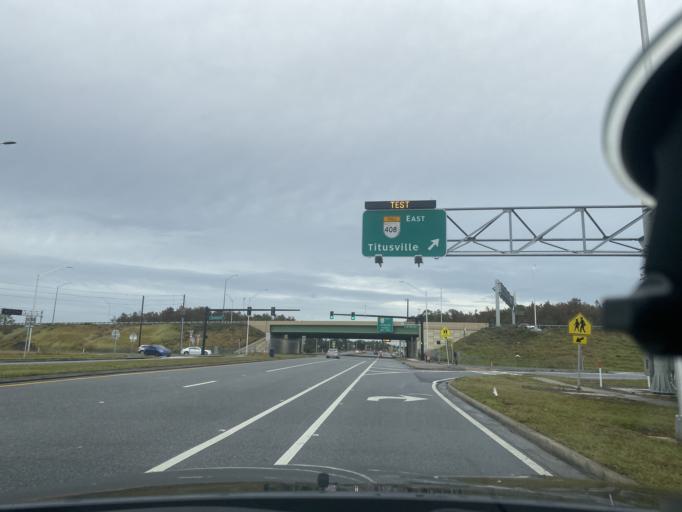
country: US
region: Florida
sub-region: Orange County
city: Alafaya
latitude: 28.5461
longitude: -81.2228
